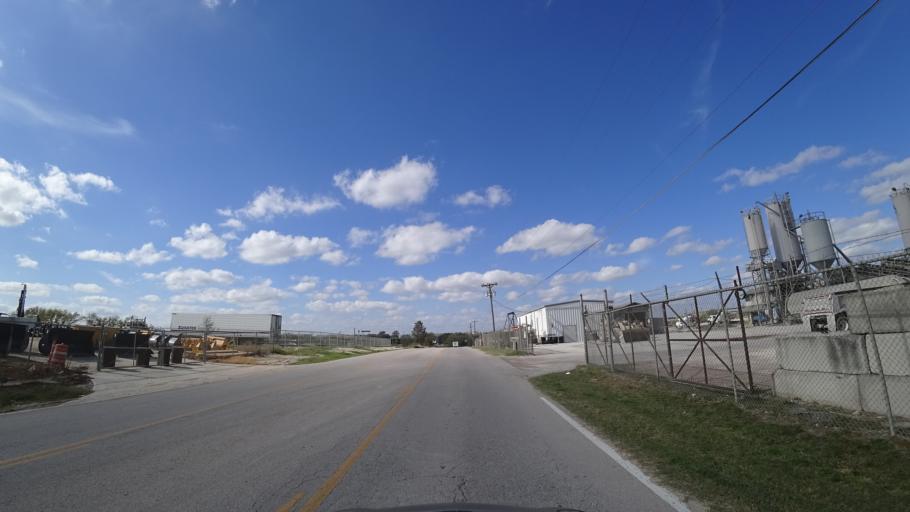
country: US
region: Texas
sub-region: Travis County
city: Windemere
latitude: 30.4690
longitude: -97.6673
